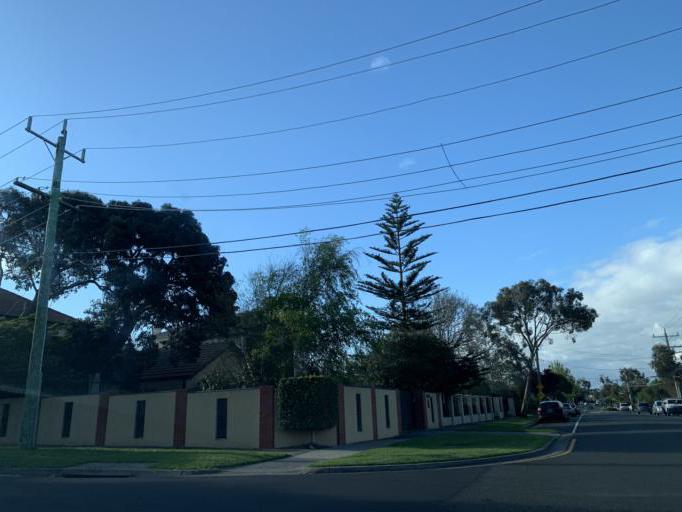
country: AU
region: Victoria
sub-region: Kingston
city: Mentone
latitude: -37.9865
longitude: 145.0598
